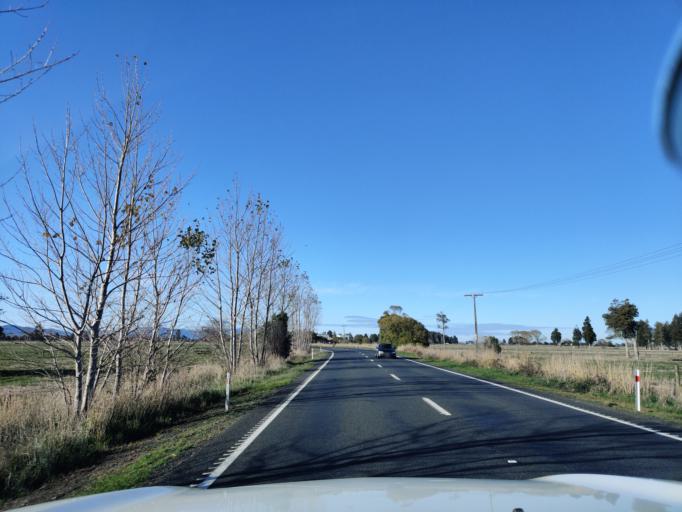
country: NZ
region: Waikato
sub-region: Hauraki District
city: Ngatea
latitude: -37.3006
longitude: 175.5582
